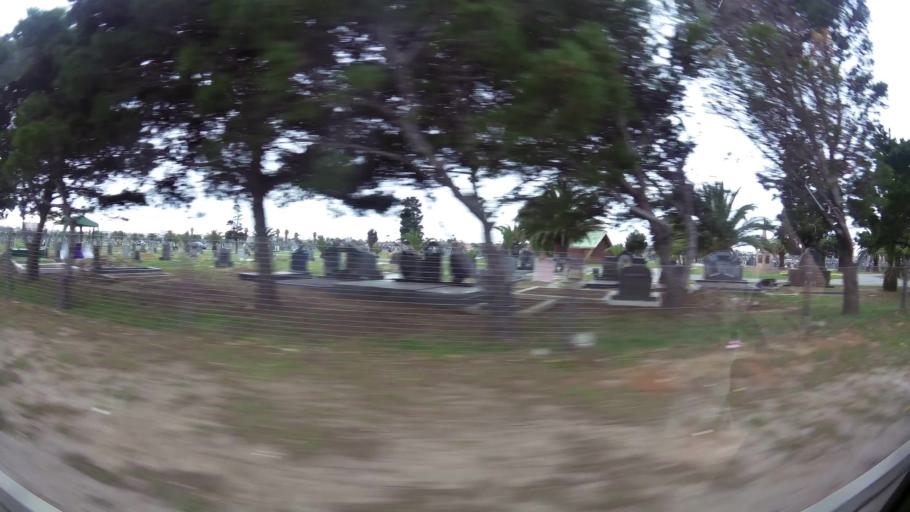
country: ZA
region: Eastern Cape
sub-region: Nelson Mandela Bay Metropolitan Municipality
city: Port Elizabeth
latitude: -33.9184
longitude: 25.5645
